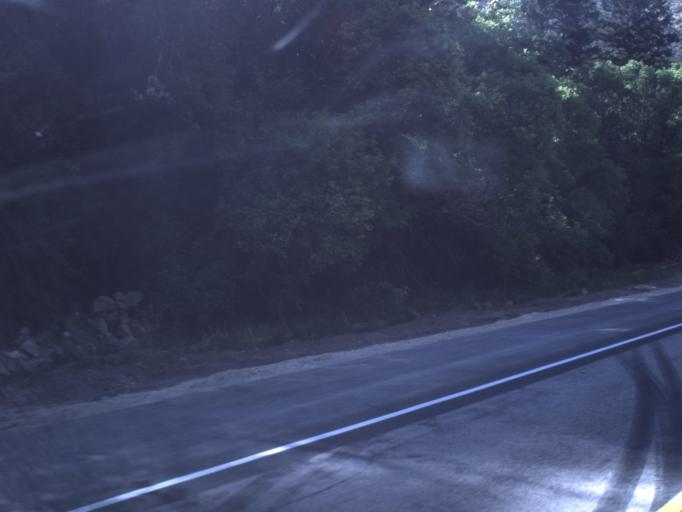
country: US
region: Utah
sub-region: Wasatch County
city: Heber
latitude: 40.3835
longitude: -111.3012
